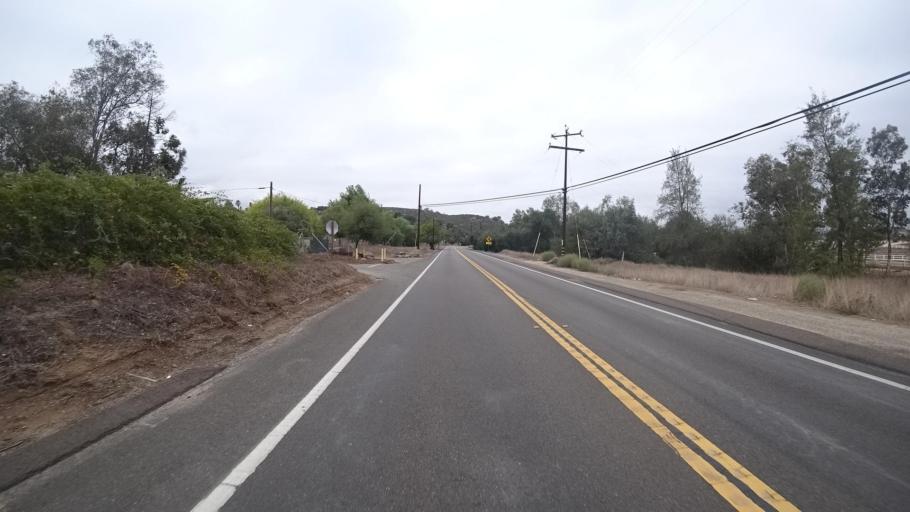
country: US
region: California
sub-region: San Diego County
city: Ramona
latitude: 33.0658
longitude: -116.8757
